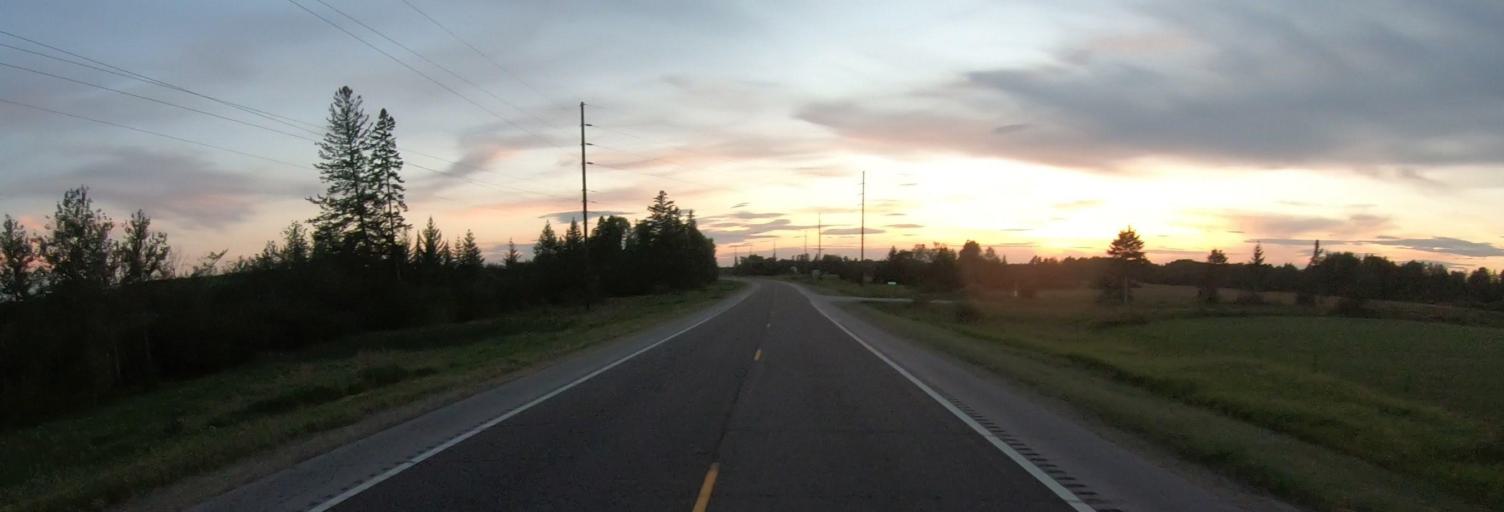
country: US
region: Minnesota
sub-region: Saint Louis County
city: Parkville
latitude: 47.8465
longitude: -92.5578
